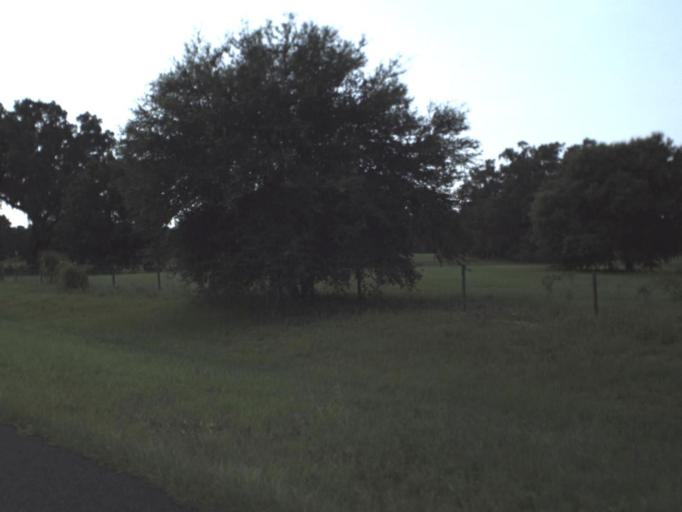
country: US
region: Florida
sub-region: Levy County
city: Inglis
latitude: 28.9807
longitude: -82.6421
